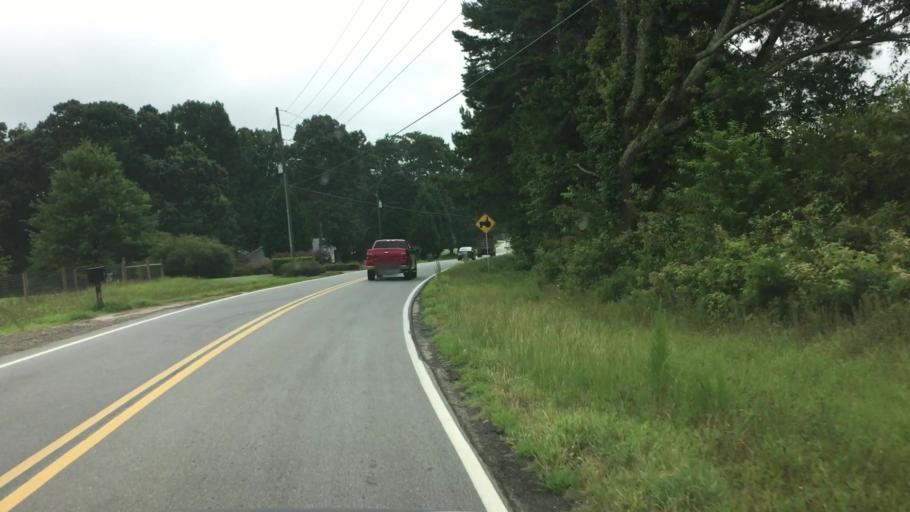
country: US
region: Georgia
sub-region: Barrow County
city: Winder
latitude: 34.0307
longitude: -83.7301
